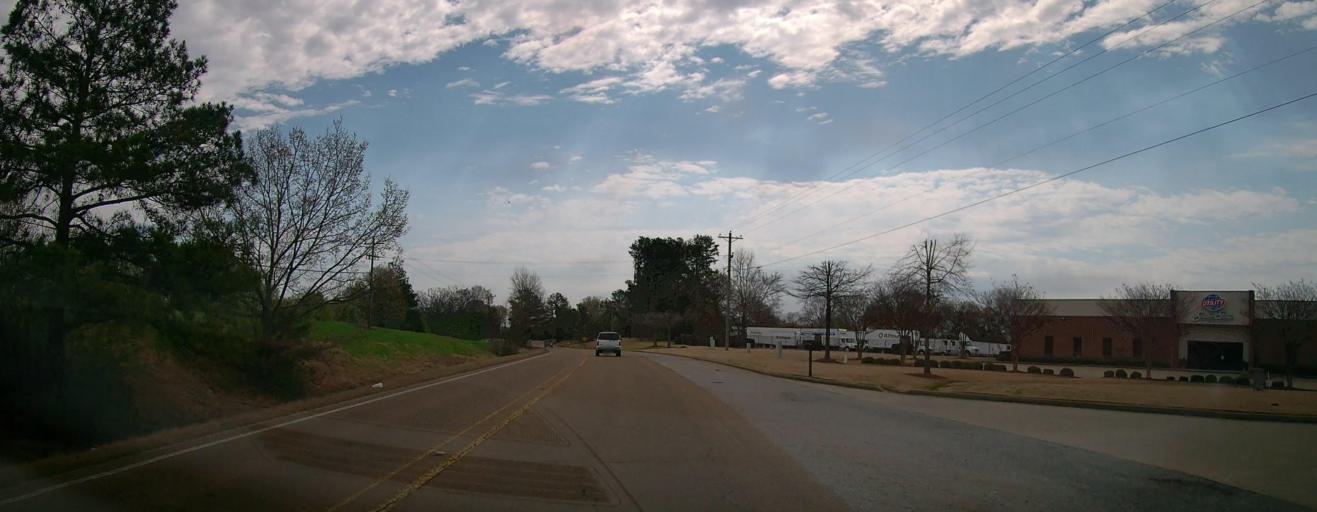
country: US
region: Mississippi
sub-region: De Soto County
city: Olive Branch
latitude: 34.9268
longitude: -89.7875
